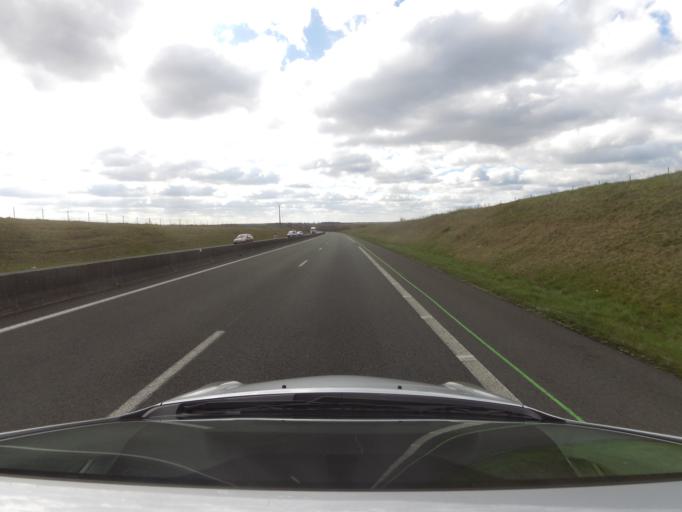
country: FR
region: Picardie
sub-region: Departement de la Somme
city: Nouvion
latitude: 50.2193
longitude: 1.7525
